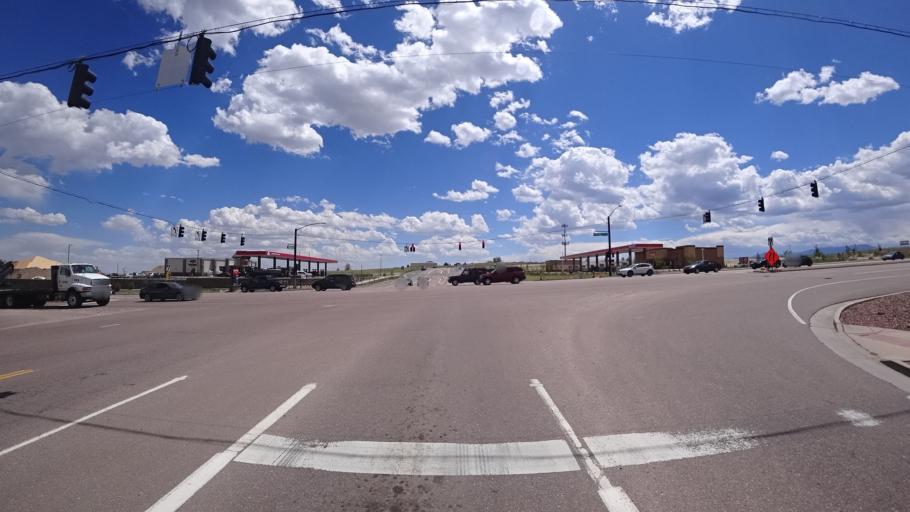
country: US
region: Colorado
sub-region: El Paso County
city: Black Forest
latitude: 38.9413
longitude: -104.7009
